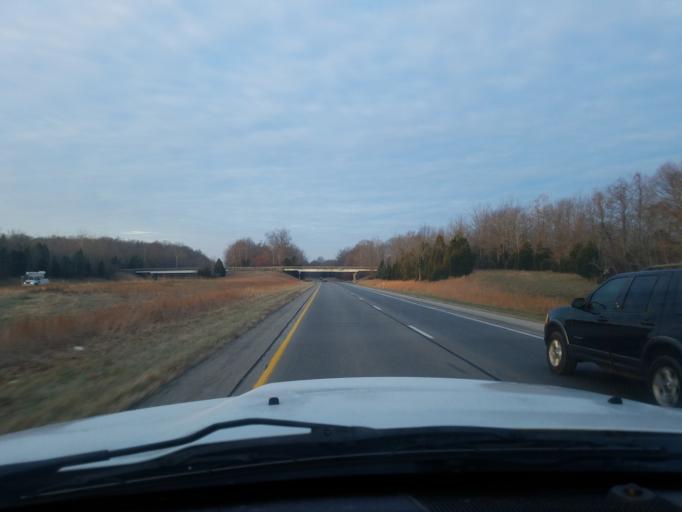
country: US
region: Indiana
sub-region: Harrison County
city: Corydon
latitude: 38.2520
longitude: -86.0483
